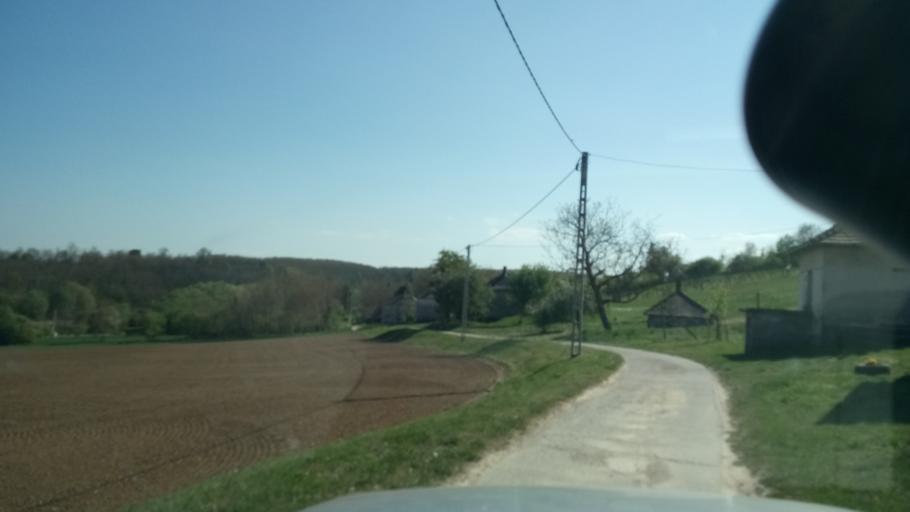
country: HU
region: Zala
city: Sarmellek
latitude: 46.6990
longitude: 17.1005
